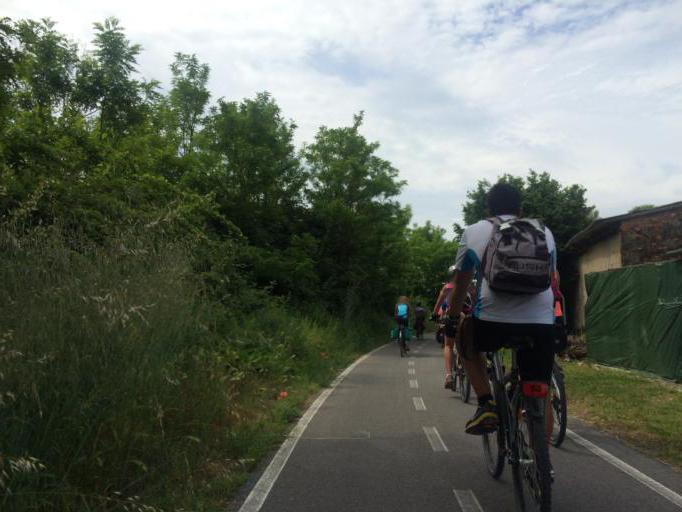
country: IT
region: Friuli Venezia Giulia
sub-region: Provincia di Udine
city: Aquileia
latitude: 45.7685
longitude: 13.3726
